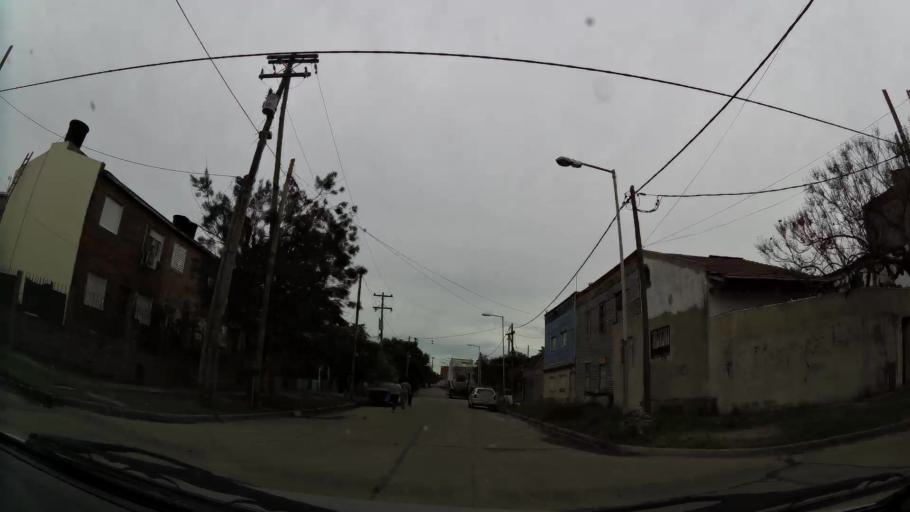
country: AR
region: Buenos Aires
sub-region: Partido de Avellaneda
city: Avellaneda
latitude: -34.6458
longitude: -58.3490
